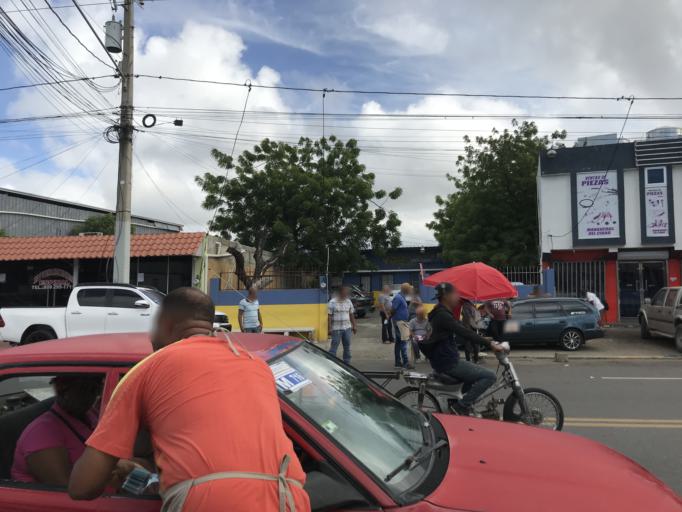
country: DO
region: Santiago
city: Santiago de los Caballeros
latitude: 19.4877
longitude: -70.7163
